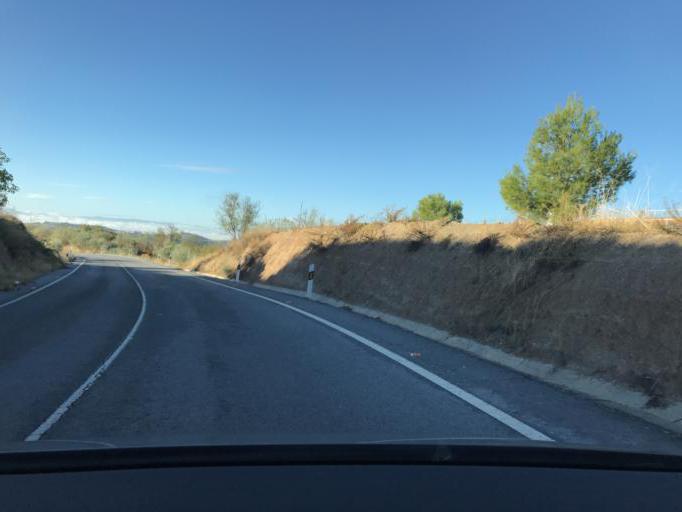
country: ES
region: Andalusia
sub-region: Provincia de Granada
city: Viznar
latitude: 37.2202
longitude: -3.5628
